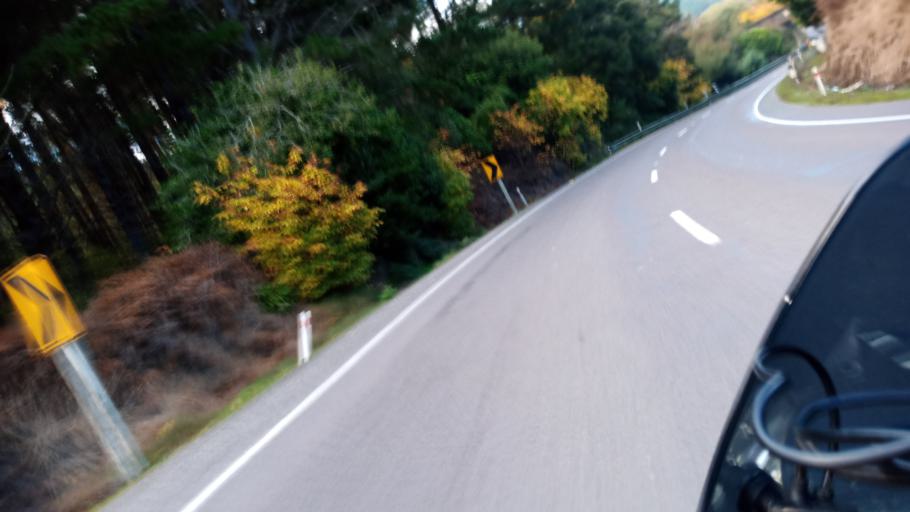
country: NZ
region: Gisborne
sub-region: Gisborne District
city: Gisborne
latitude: -38.8380
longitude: 177.8970
